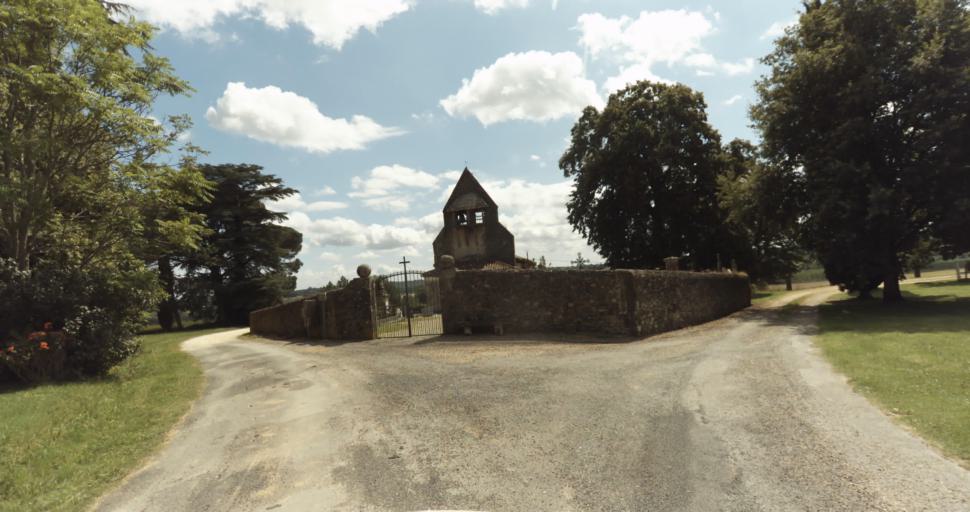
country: FR
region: Aquitaine
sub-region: Departement de la Gironde
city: Bazas
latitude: 44.4581
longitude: -0.1735
